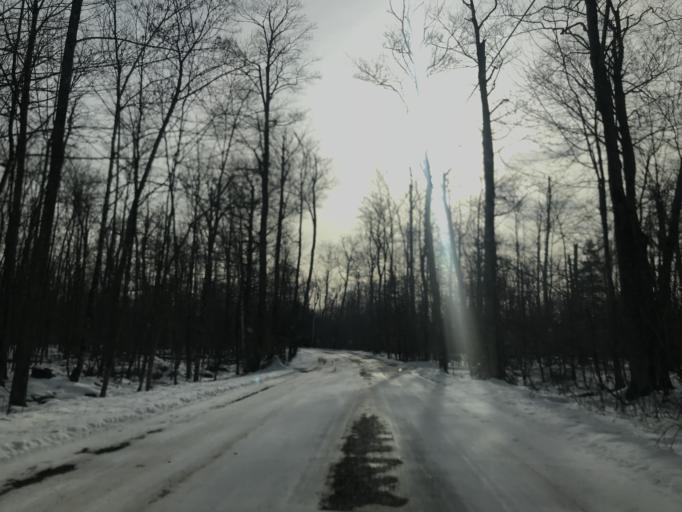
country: US
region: Wisconsin
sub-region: Door County
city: Sturgeon Bay
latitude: 45.1454
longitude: -87.0539
